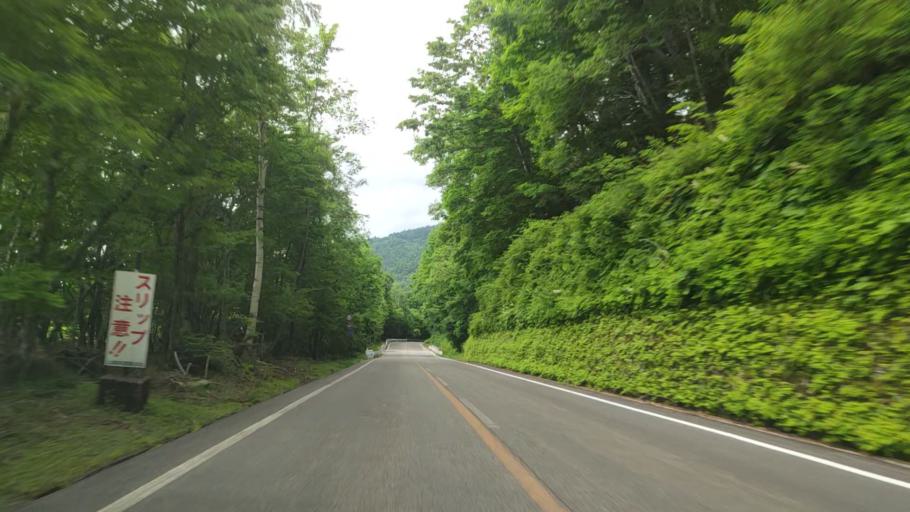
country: JP
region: Yamanashi
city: Fujikawaguchiko
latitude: 35.4137
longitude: 138.7352
